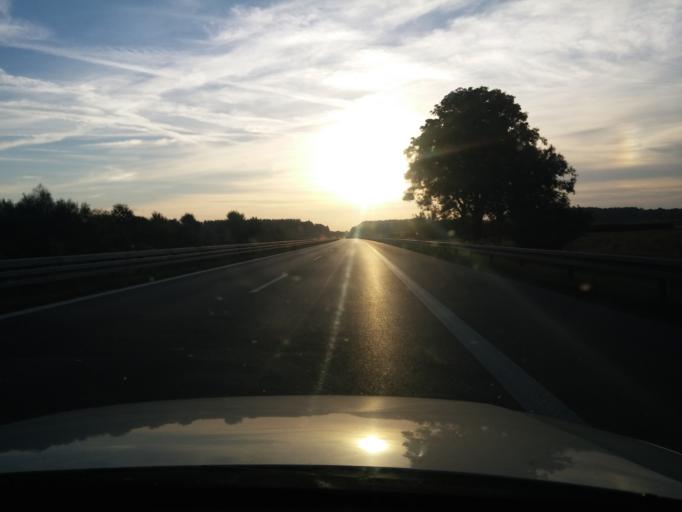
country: DE
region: Bavaria
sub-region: Swabia
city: Wiedergeltingen
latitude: 48.0267
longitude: 10.6847
